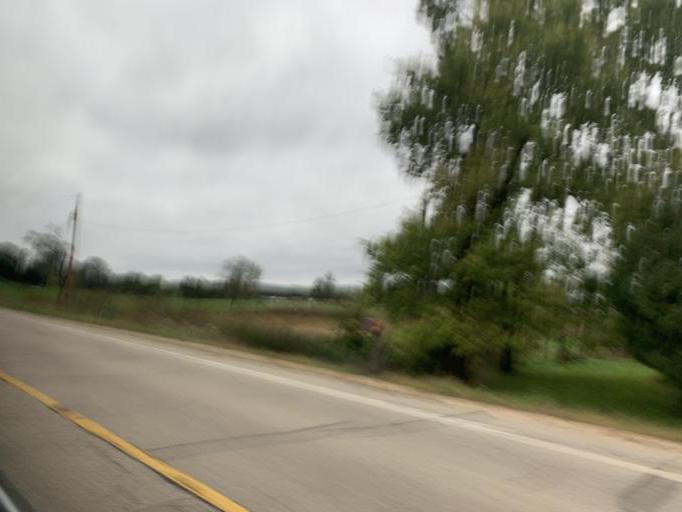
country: US
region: Wisconsin
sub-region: Grant County
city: Boscobel
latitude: 43.2054
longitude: -90.6118
